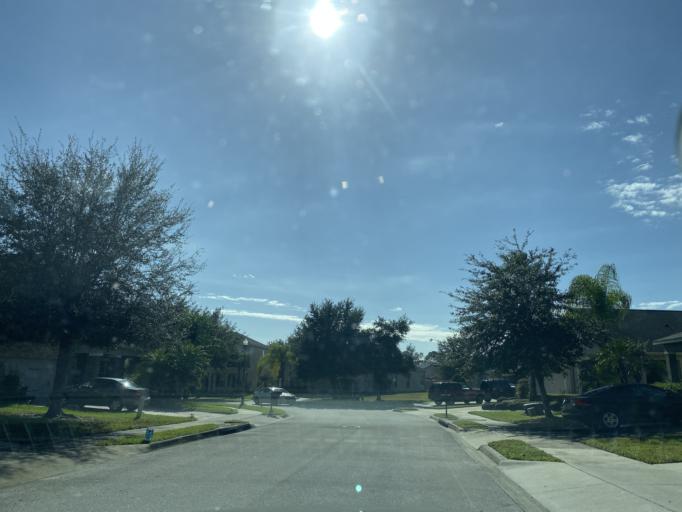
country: US
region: Florida
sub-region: Seminole County
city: Goldenrod
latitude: 28.6142
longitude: -81.2611
